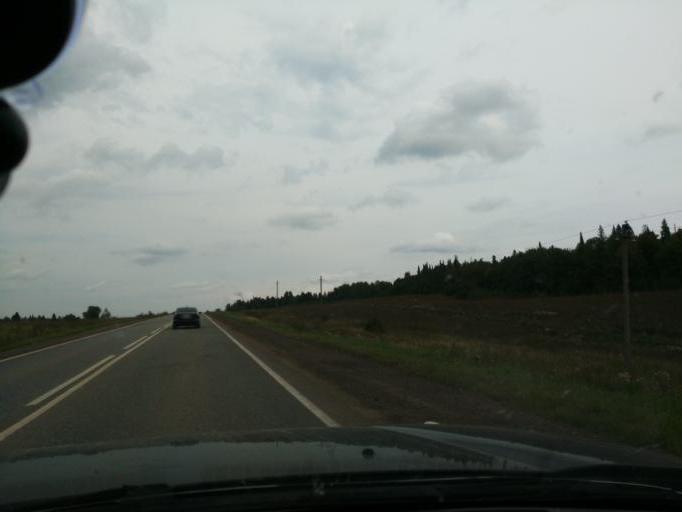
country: RU
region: Perm
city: Kuyeda
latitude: 56.4670
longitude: 55.6742
